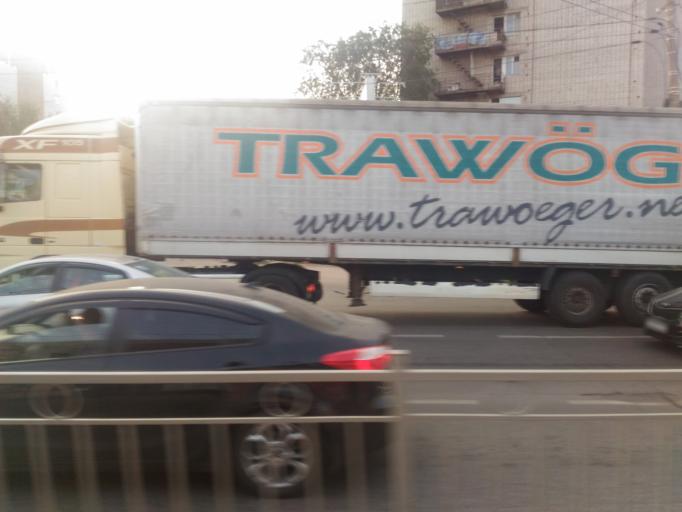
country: RU
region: Ulyanovsk
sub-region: Ulyanovskiy Rayon
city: Ulyanovsk
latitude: 54.2863
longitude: 48.3028
